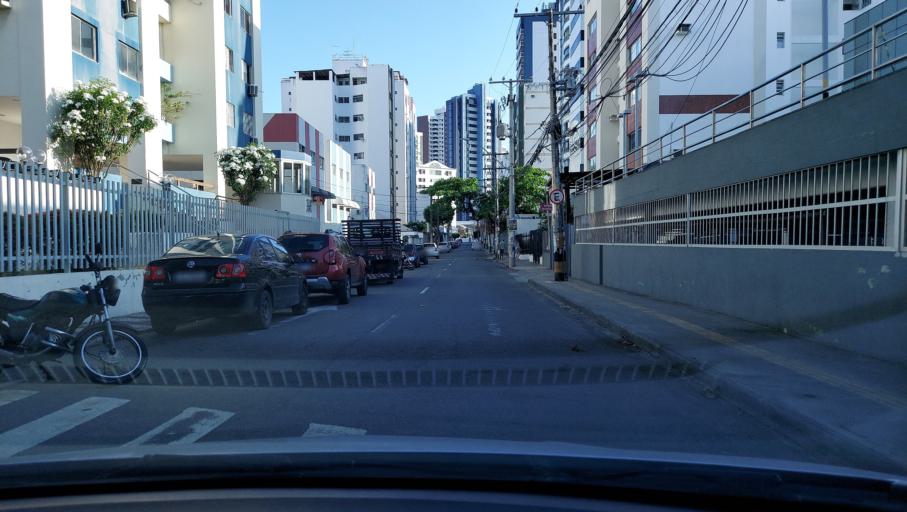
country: BR
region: Bahia
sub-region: Salvador
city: Salvador
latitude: -12.9941
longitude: -38.4540
